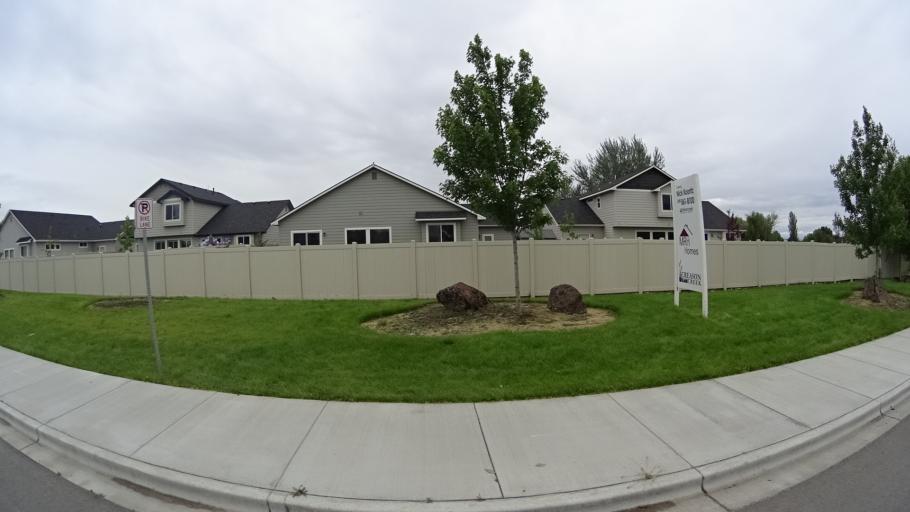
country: US
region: Idaho
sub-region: Ada County
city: Meridian
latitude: 43.6338
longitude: -116.4110
